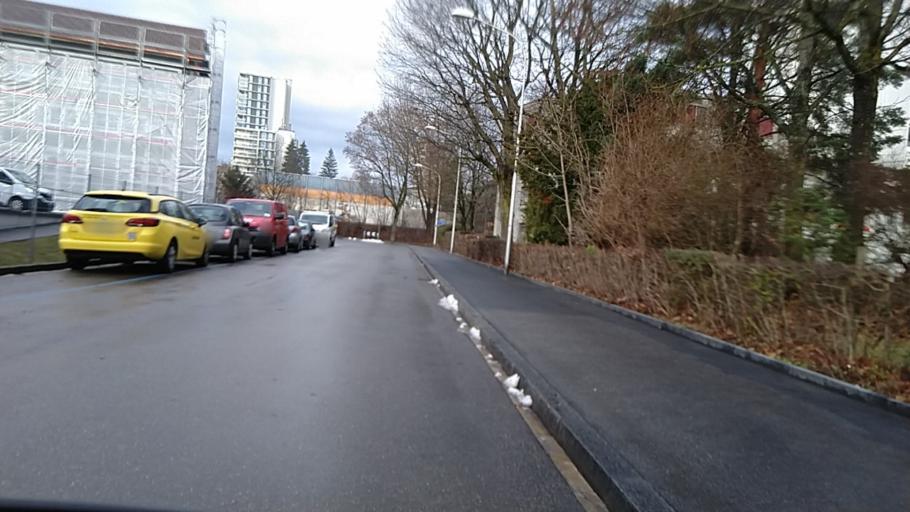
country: CH
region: Bern
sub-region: Bern-Mittelland District
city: Koniz
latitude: 46.9353
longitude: 7.3869
